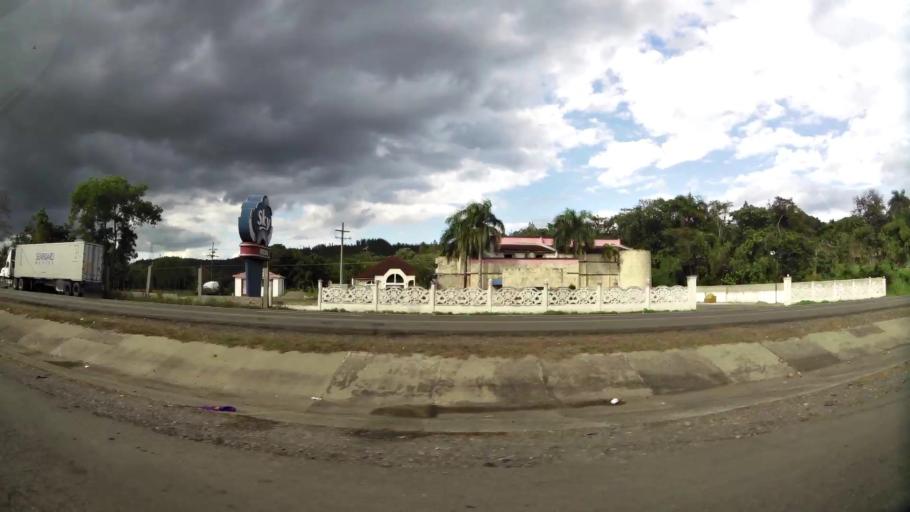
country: DO
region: Monsenor Nouel
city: Bonao
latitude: 18.9705
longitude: -70.4181
